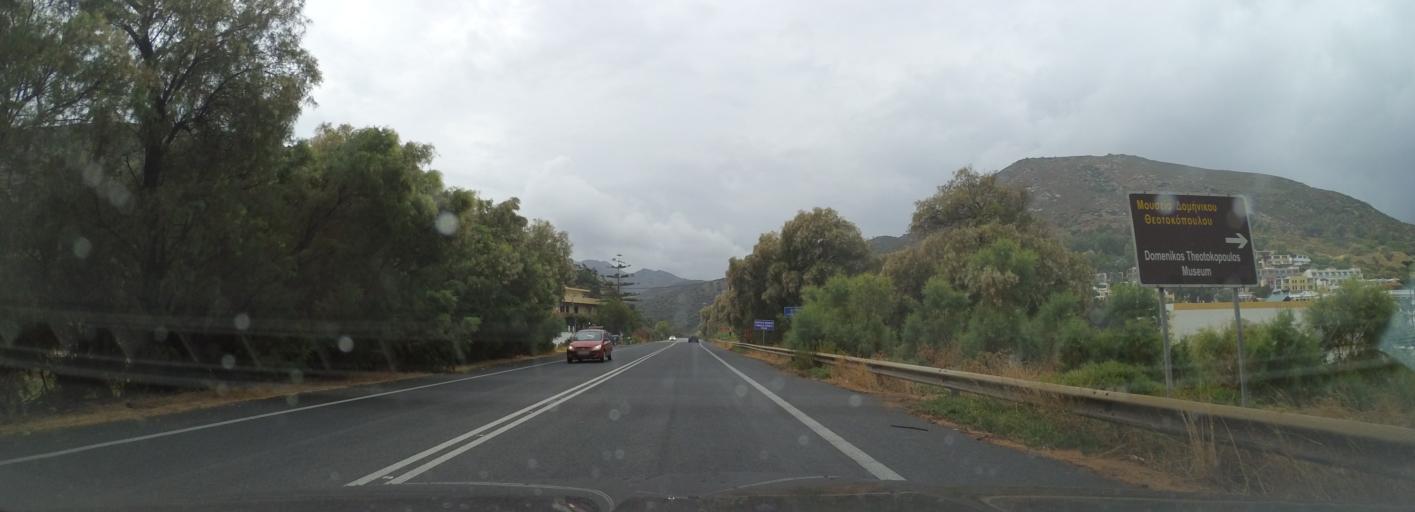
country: GR
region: Crete
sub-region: Nomos Irakleiou
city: Tilisos
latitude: 35.4013
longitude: 24.9556
